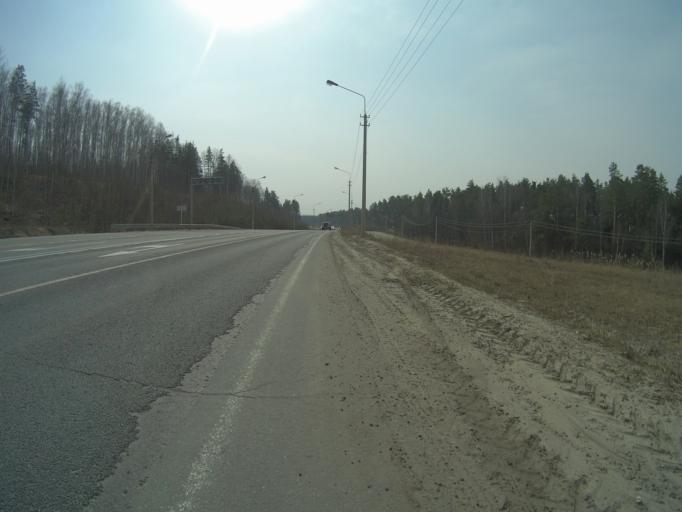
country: RU
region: Vladimir
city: Kommunar
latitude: 56.0551
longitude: 40.4395
